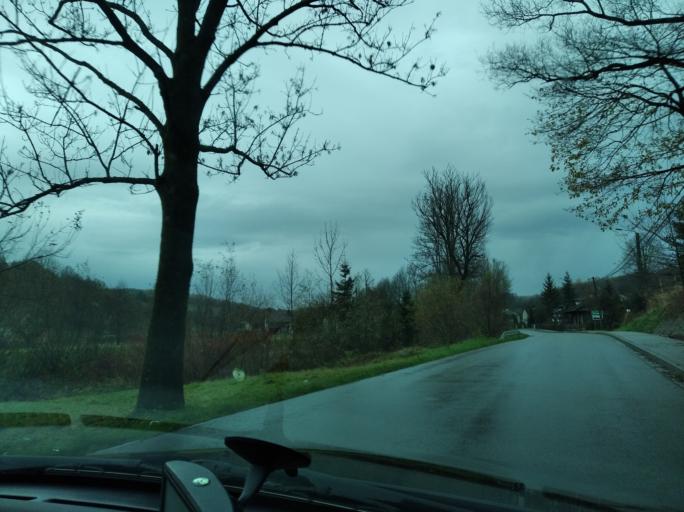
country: PL
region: Subcarpathian Voivodeship
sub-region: Powiat rzeszowski
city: Straszydle
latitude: 49.9163
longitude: 21.9579
